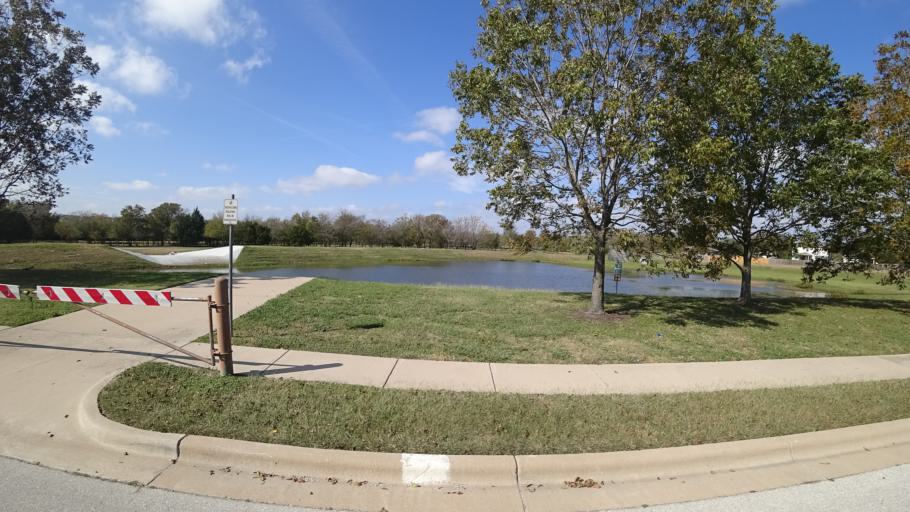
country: US
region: Texas
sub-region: Travis County
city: Pflugerville
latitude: 30.4180
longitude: -97.6396
